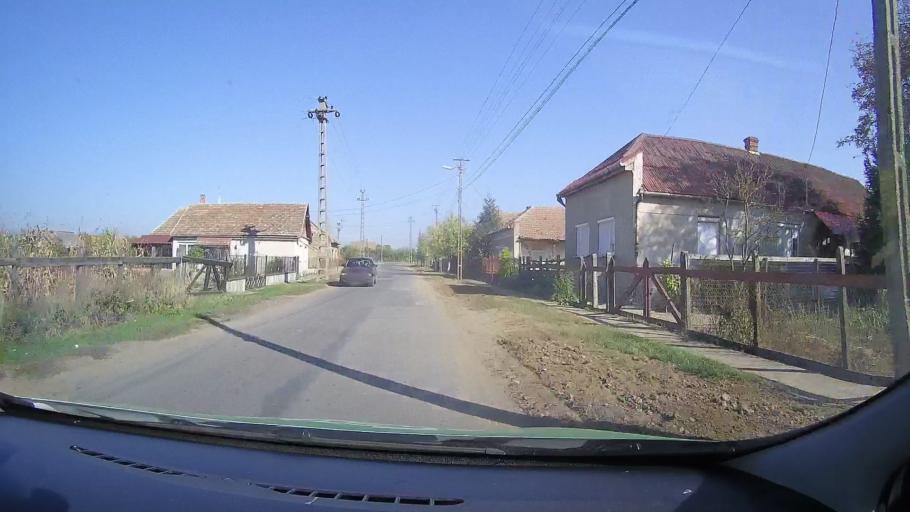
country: RO
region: Satu Mare
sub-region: Comuna Ciumesti
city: Ciumesti
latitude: 47.6684
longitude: 22.3386
